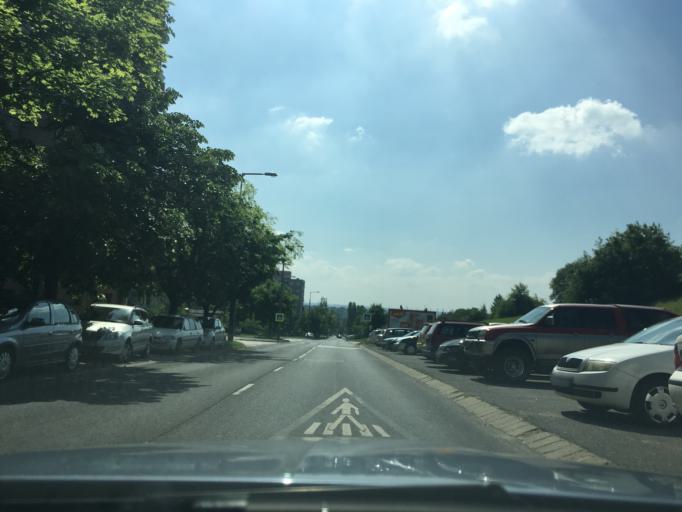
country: HU
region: Budapest
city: Budapest XII. keruelet
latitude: 47.4672
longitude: 18.9998
